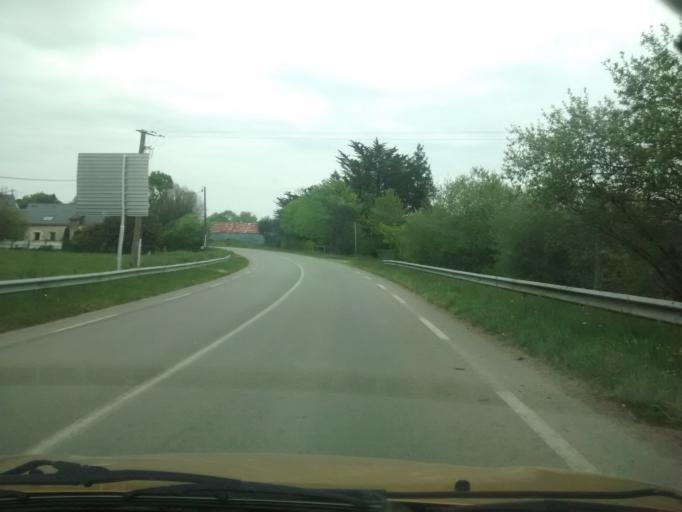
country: FR
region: Brittany
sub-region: Departement du Morbihan
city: Ambon
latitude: 47.5915
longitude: -2.5489
